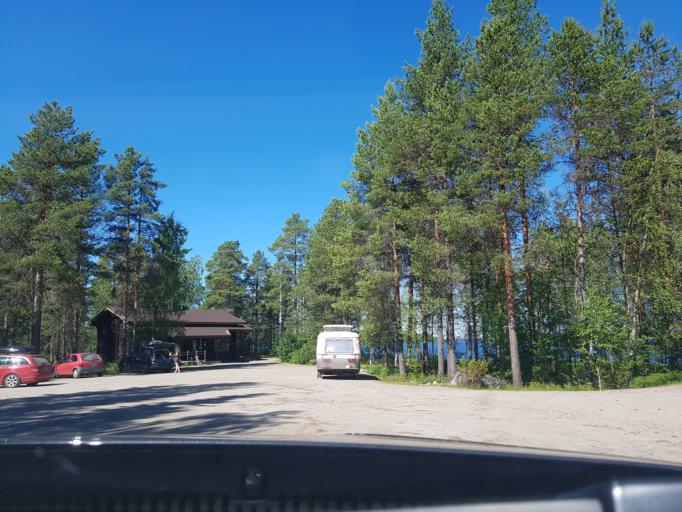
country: FI
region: Kainuu
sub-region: Kehys-Kainuu
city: Kuhmo
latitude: 64.1954
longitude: 29.5950
